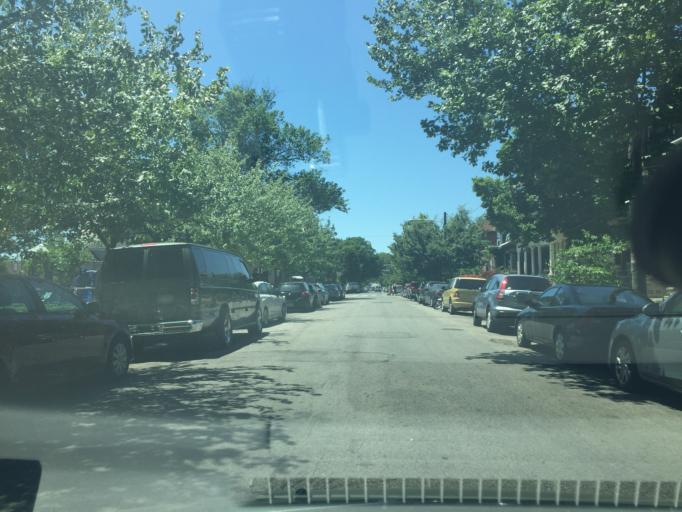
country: US
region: Pennsylvania
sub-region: Delaware County
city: Millbourne
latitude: 39.9483
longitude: -75.2222
